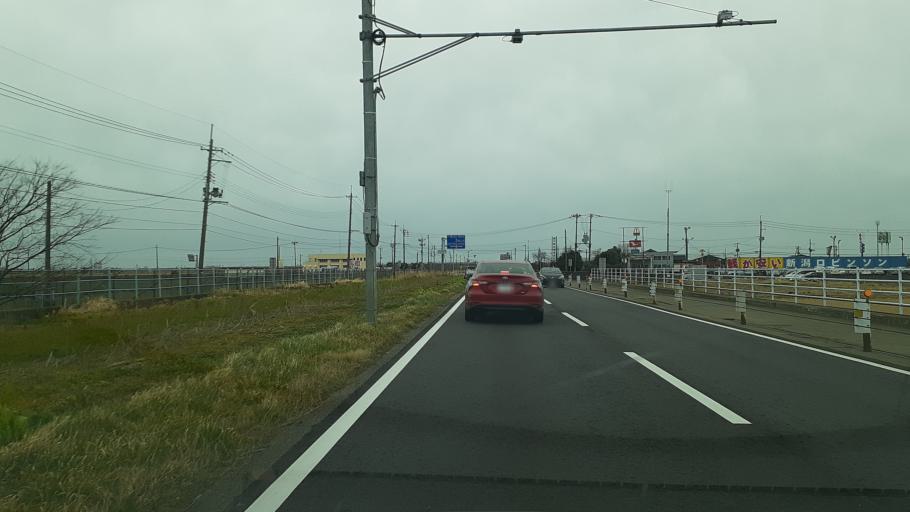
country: JP
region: Niigata
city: Niitsu-honcho
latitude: 37.8134
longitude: 139.1004
